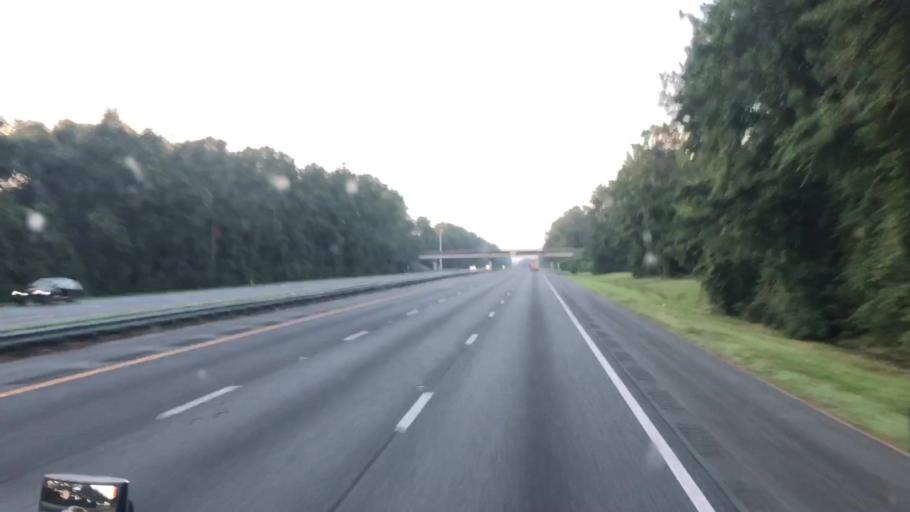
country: US
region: Florida
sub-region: Alachua County
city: High Springs
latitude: 29.9547
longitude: -82.5699
